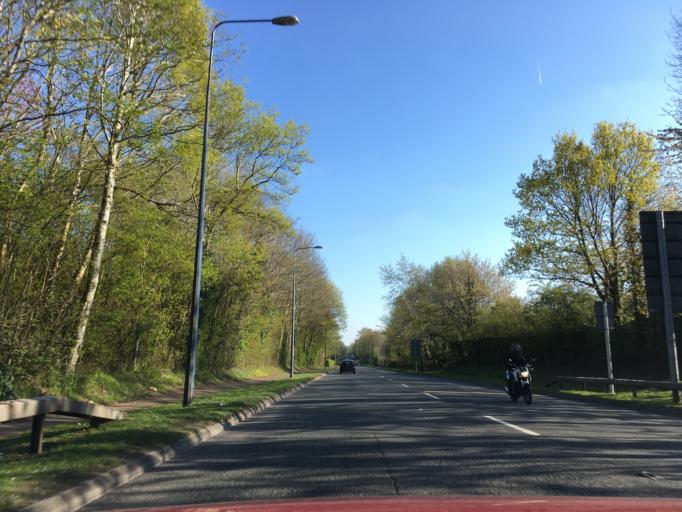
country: GB
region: Wales
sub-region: Torfaen County Borough
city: Cwmbran
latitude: 51.6418
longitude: -3.0219
